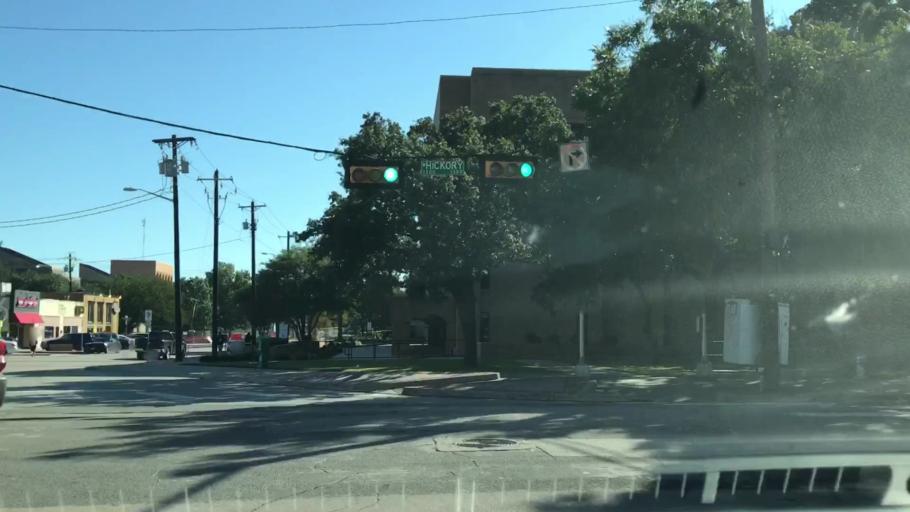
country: US
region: Texas
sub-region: Denton County
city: Denton
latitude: 33.2147
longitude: -97.1464
